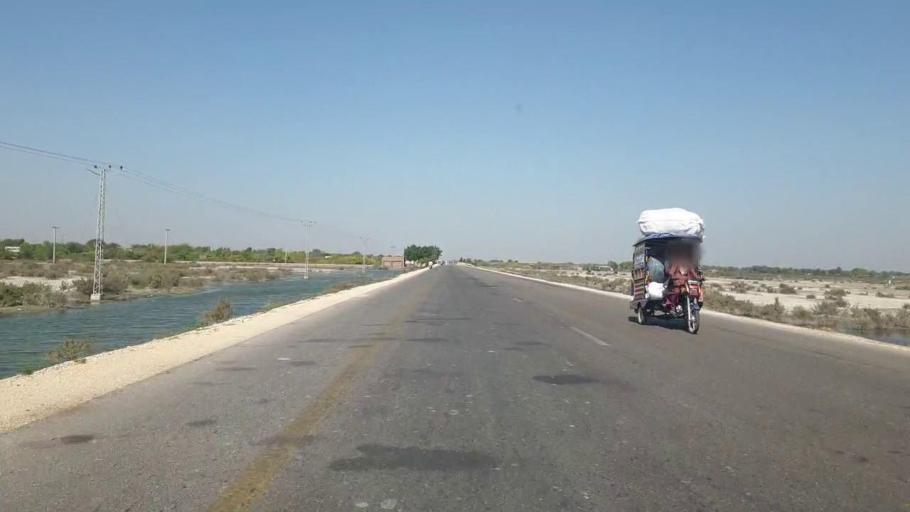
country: PK
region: Sindh
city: Talhar
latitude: 24.8456
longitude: 68.8163
